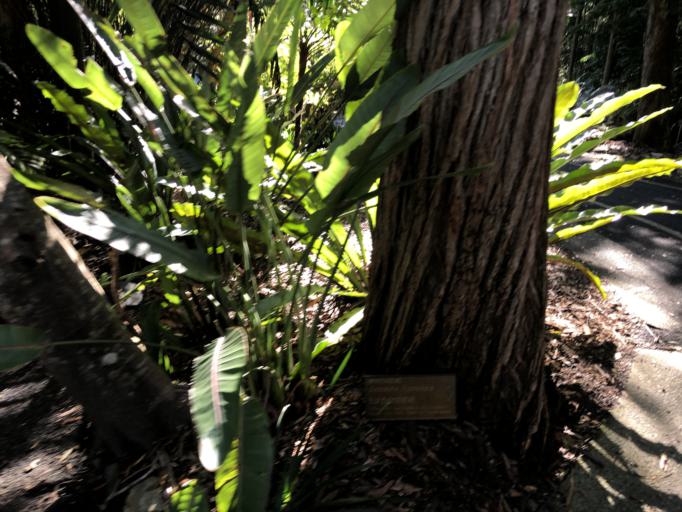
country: AU
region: New South Wales
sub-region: Coffs Harbour
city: Coffs Harbour
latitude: -30.2980
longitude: 153.1248
